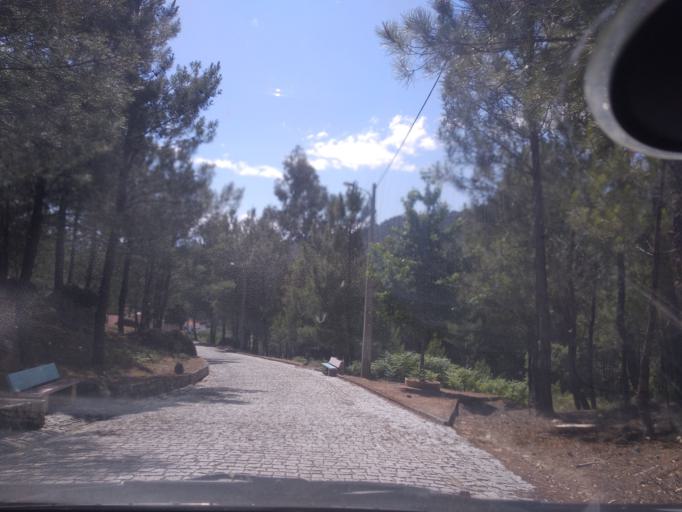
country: PT
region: Castelo Branco
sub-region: Concelho do Fundao
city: Fundao
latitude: 40.2086
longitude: -7.4401
